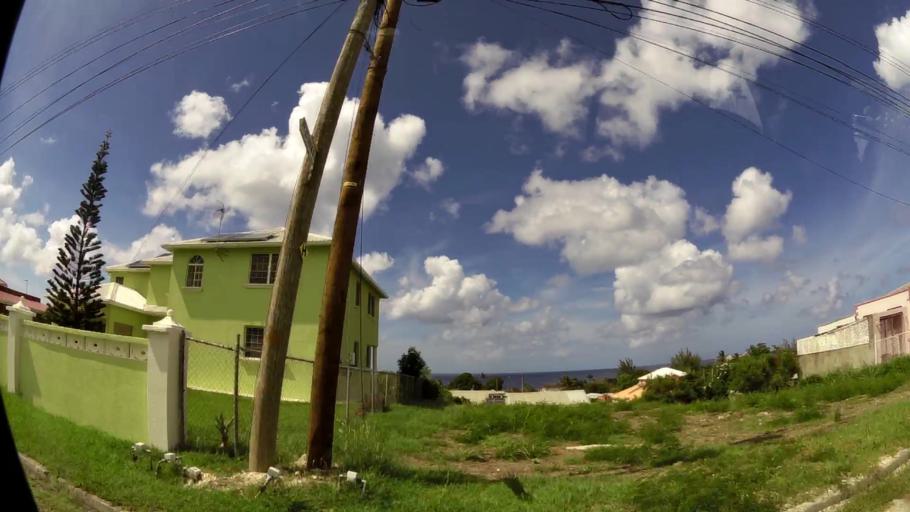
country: BB
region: Saint James
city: Holetown
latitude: 13.1532
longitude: -59.6350
